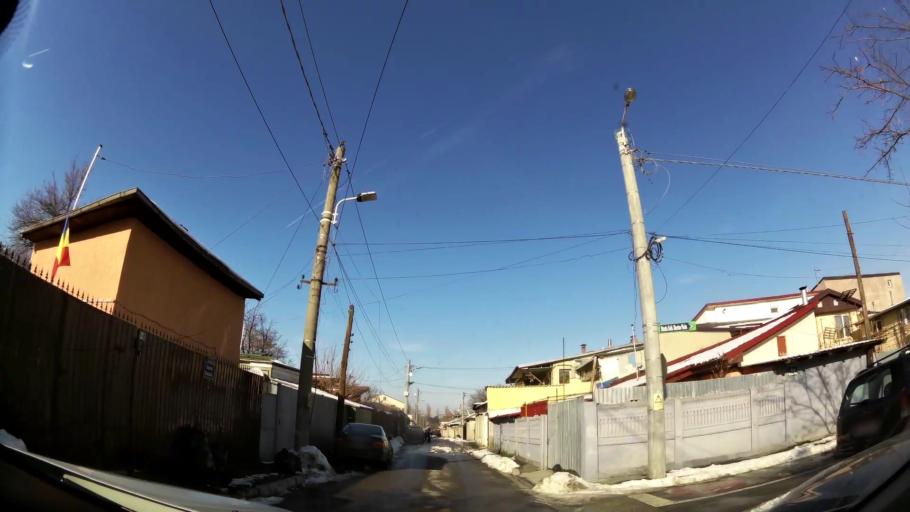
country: RO
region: Ilfov
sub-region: Comuna Fundeni-Dobroesti
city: Fundeni
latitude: 44.4725
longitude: 26.1293
